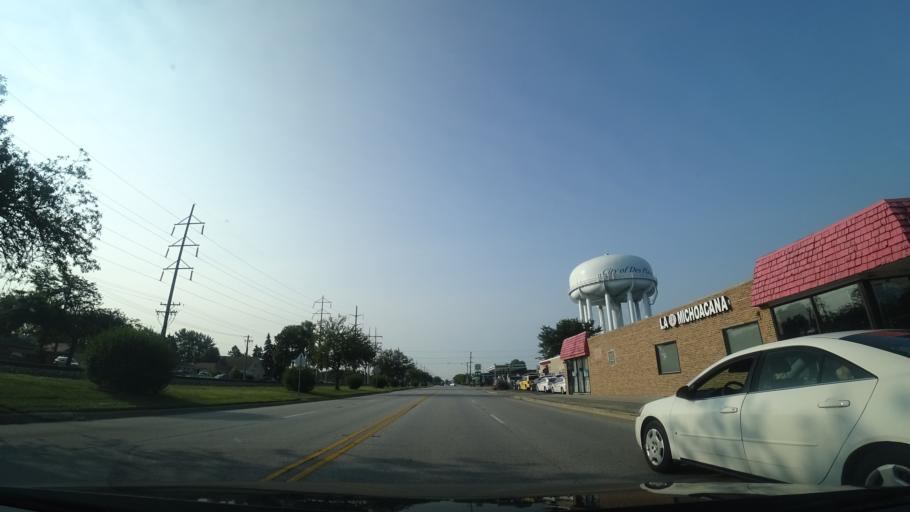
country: US
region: Illinois
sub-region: Cook County
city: Des Plaines
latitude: 42.0182
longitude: -87.8889
